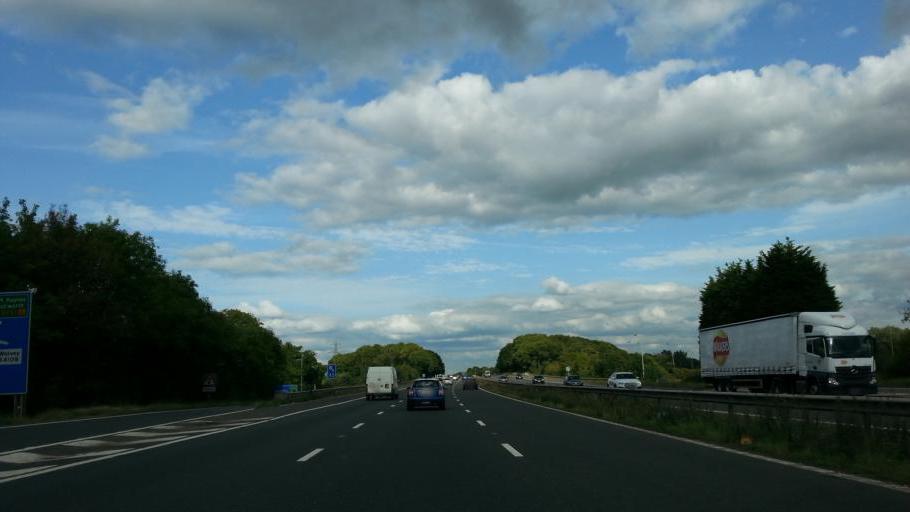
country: GB
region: England
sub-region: Leicestershire
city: Hinckley
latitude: 52.5138
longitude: -1.3666
